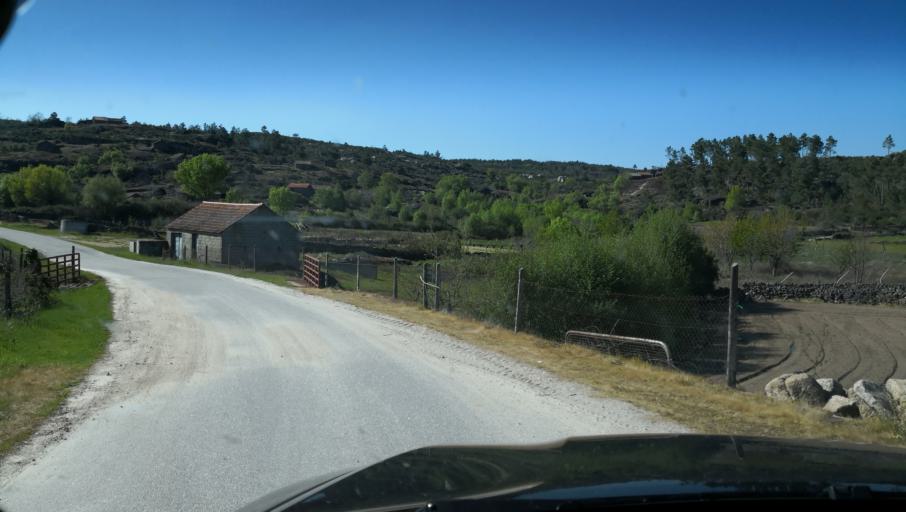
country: PT
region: Vila Real
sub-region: Sabrosa
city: Sabrosa
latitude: 41.2996
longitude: -7.6403
